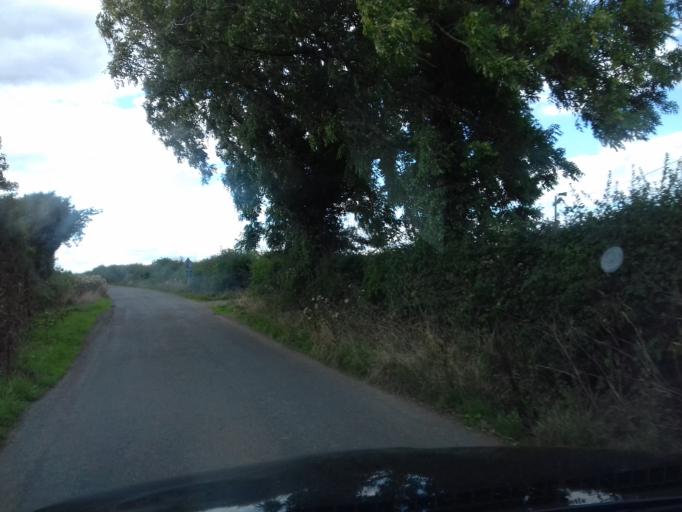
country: IE
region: Leinster
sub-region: Kilkenny
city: Graiguenamanagh
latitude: 52.5710
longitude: -7.0029
